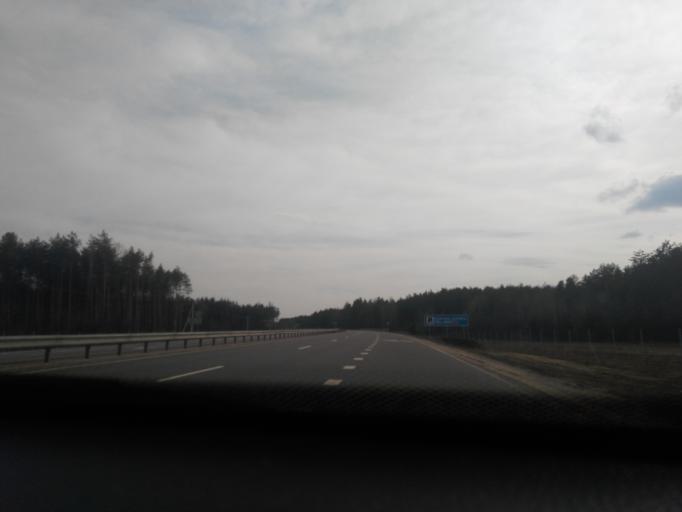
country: BY
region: Mogilev
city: Babruysk
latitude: 53.1098
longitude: 29.3533
